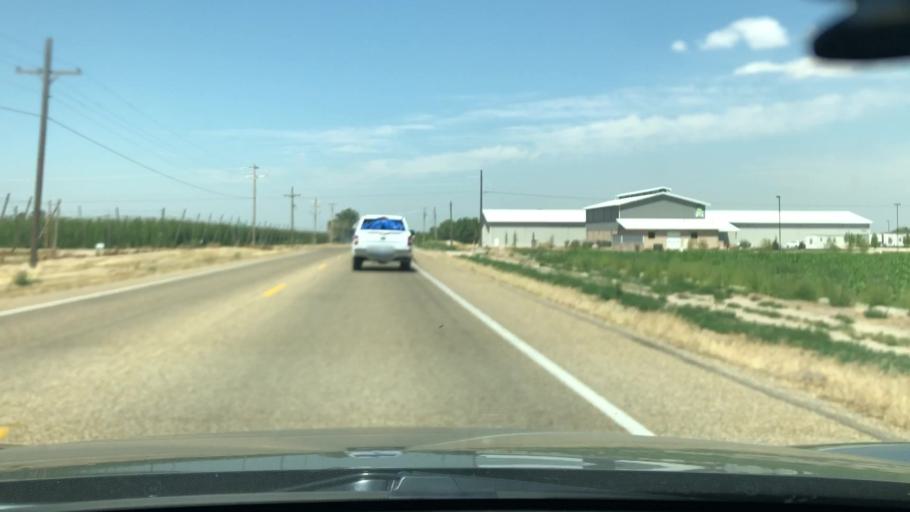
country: US
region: Idaho
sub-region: Canyon County
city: Wilder
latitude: 43.7043
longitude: -116.9120
